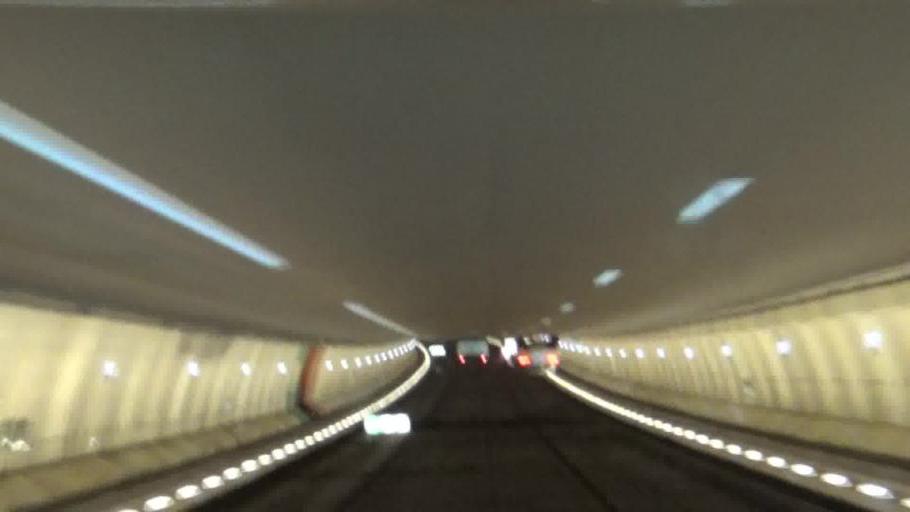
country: FR
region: Ile-de-France
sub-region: Departement des Yvelines
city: La Celle-Saint-Cloud
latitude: 48.8574
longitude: 2.1561
